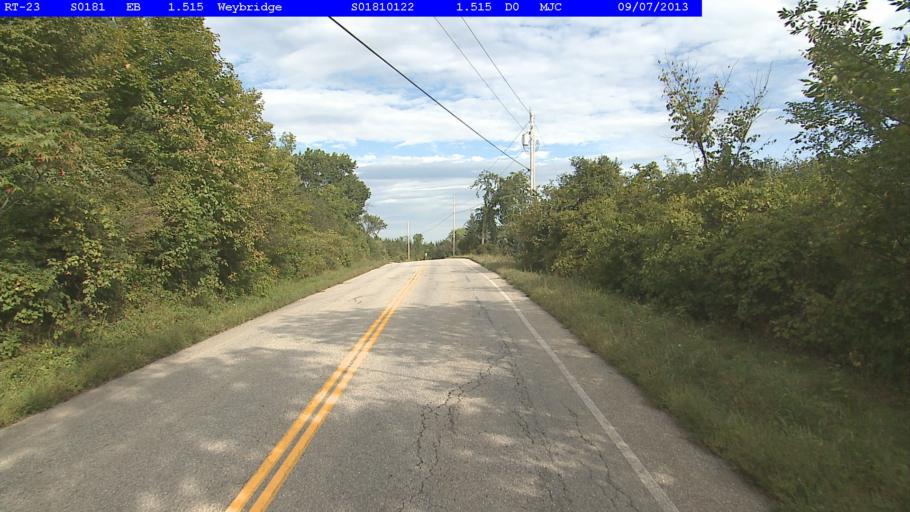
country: US
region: Vermont
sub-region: Addison County
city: Middlebury (village)
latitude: 44.0337
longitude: -73.2044
